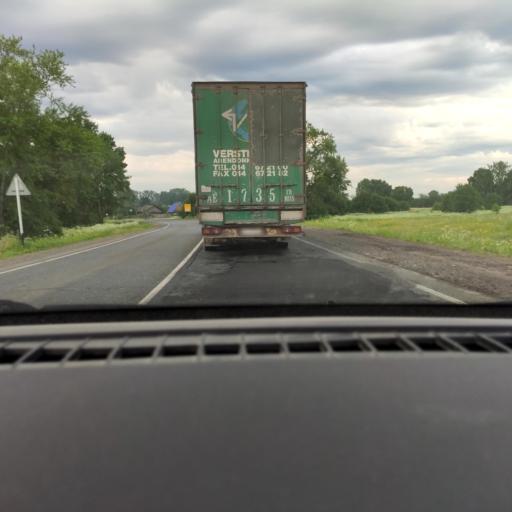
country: RU
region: Udmurtiya
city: Votkinsk
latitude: 57.3622
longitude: 54.4210
